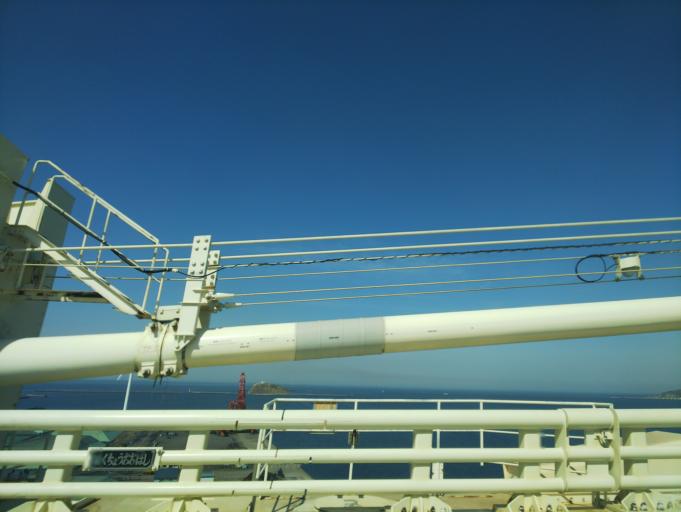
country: JP
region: Hokkaido
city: Muroran
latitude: 42.3468
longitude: 140.9491
